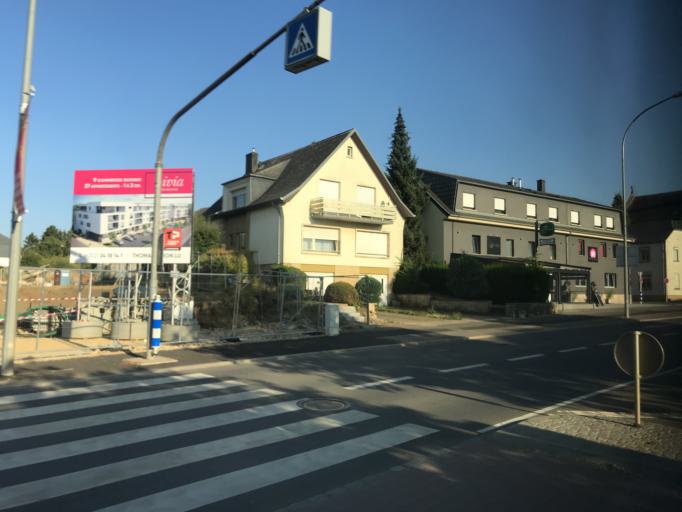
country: LU
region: Luxembourg
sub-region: Canton de Luxembourg
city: Alzingen
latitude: 49.5696
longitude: 6.1610
